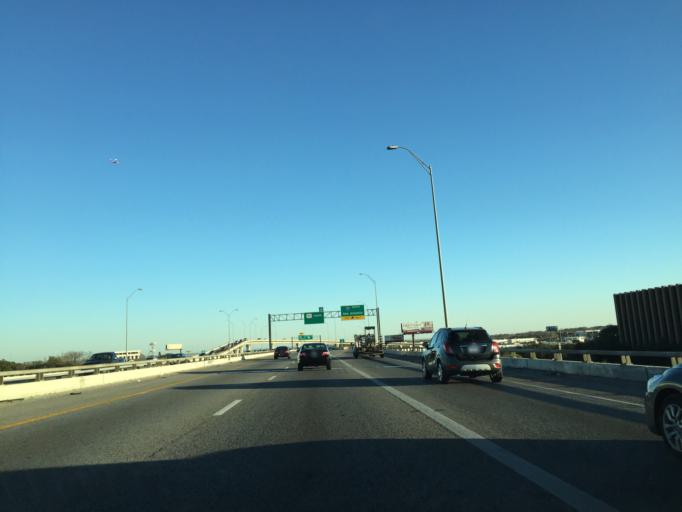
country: US
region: Texas
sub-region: Travis County
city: Austin
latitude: 30.3424
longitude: -97.7037
